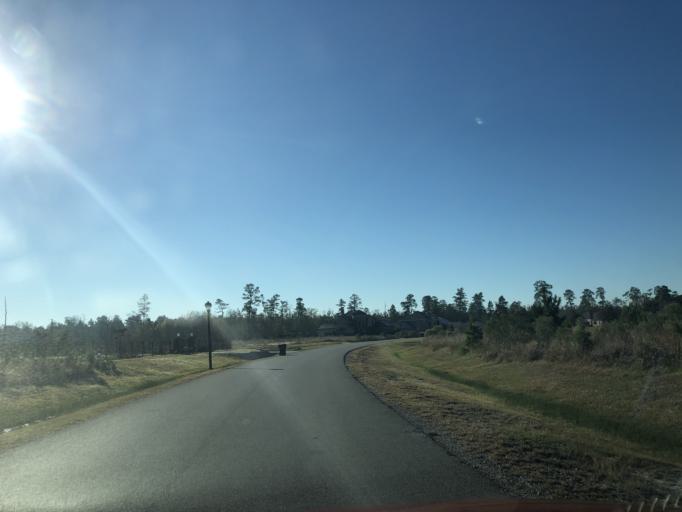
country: US
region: Texas
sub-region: Montgomery County
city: Porter Heights
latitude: 30.0741
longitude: -95.3185
